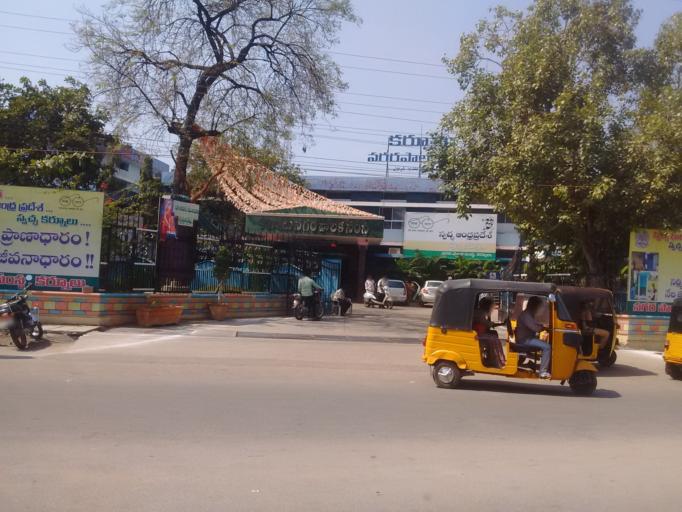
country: IN
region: Telangana
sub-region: Mahbubnagar
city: Alampur
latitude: 15.8368
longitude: 78.0412
